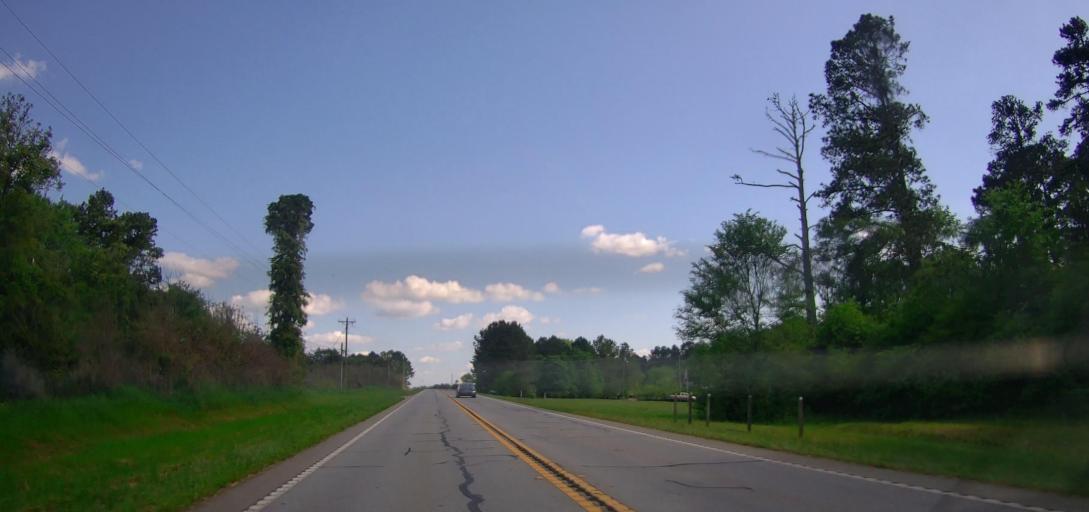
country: US
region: Georgia
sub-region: Greene County
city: Greensboro
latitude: 33.6029
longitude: -83.3072
